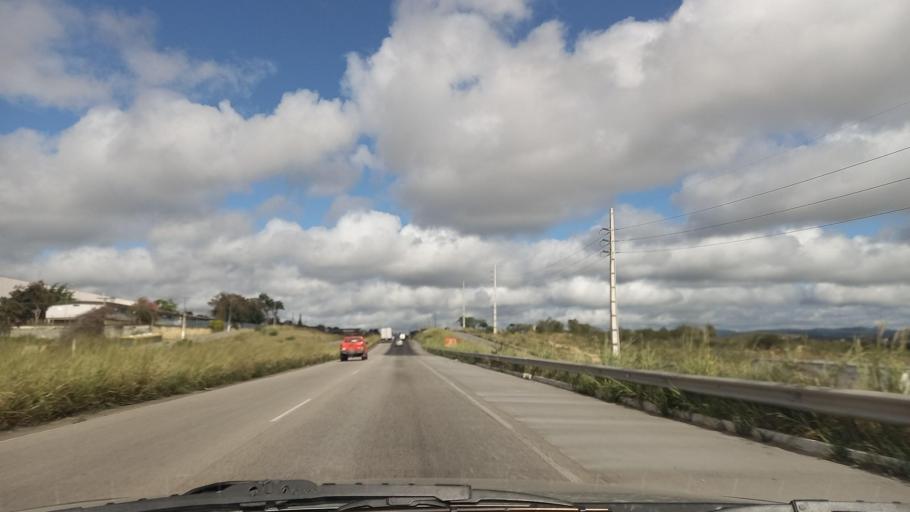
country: BR
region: Pernambuco
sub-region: Caruaru
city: Caruaru
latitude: -8.3053
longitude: -36.0129
